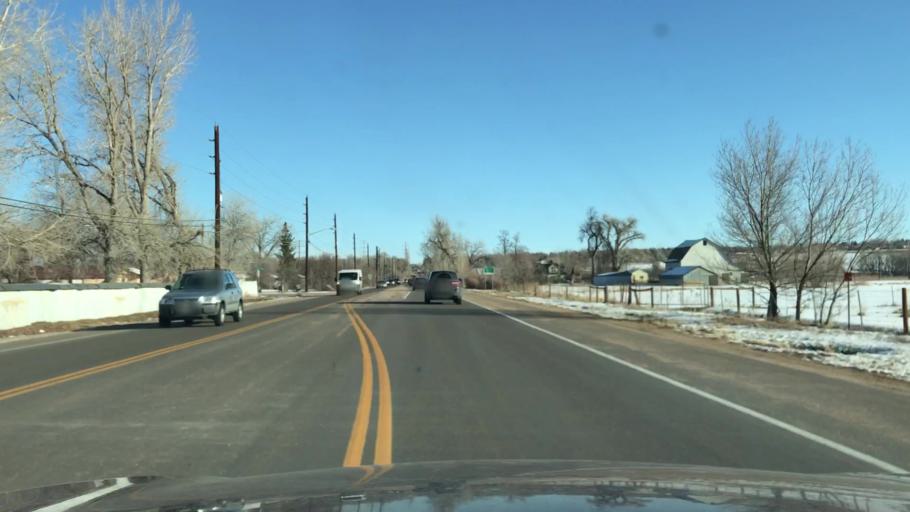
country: US
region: Colorado
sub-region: Boulder County
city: Gunbarrel
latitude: 40.0446
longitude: -105.1783
